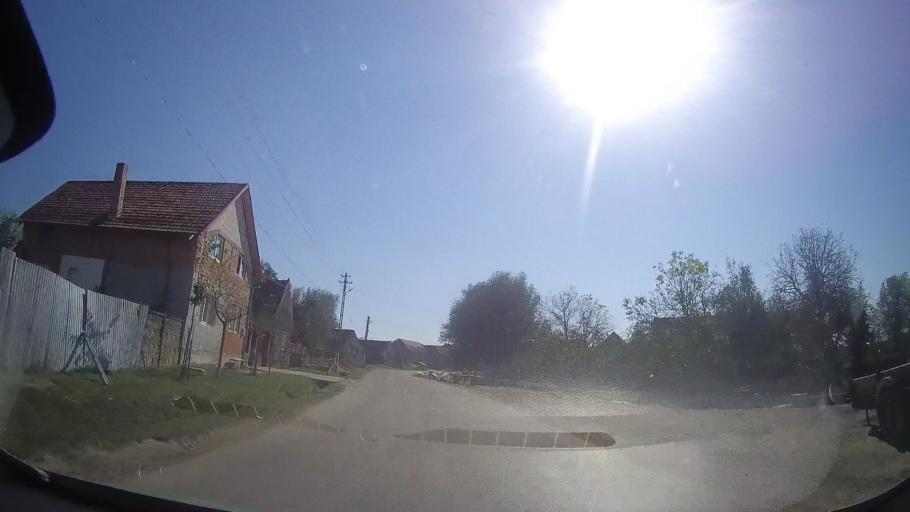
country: RO
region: Timis
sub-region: Comuna Bethausen
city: Bethausen
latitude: 45.8671
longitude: 21.9669
